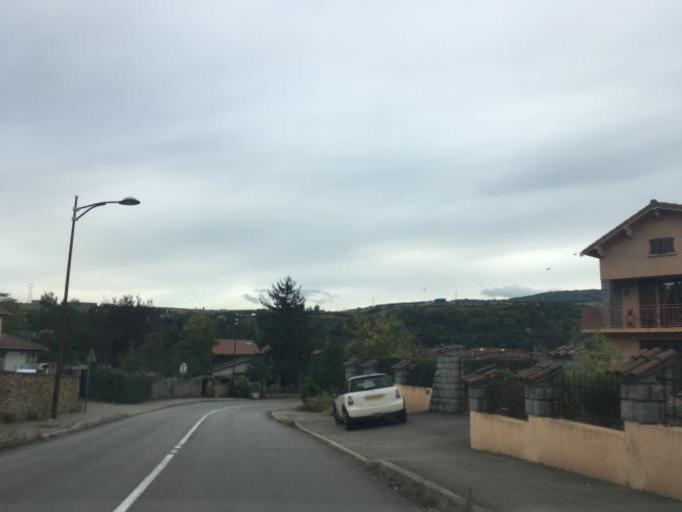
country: FR
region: Rhone-Alpes
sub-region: Departement de la Loire
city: Chateauneuf
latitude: 45.5425
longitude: 4.6406
